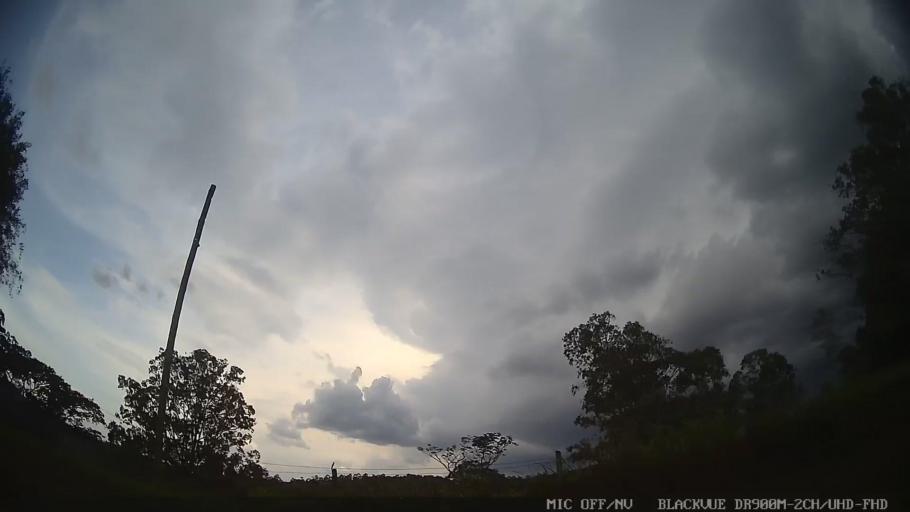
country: BR
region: Sao Paulo
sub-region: Itatiba
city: Itatiba
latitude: -22.9423
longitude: -46.8087
